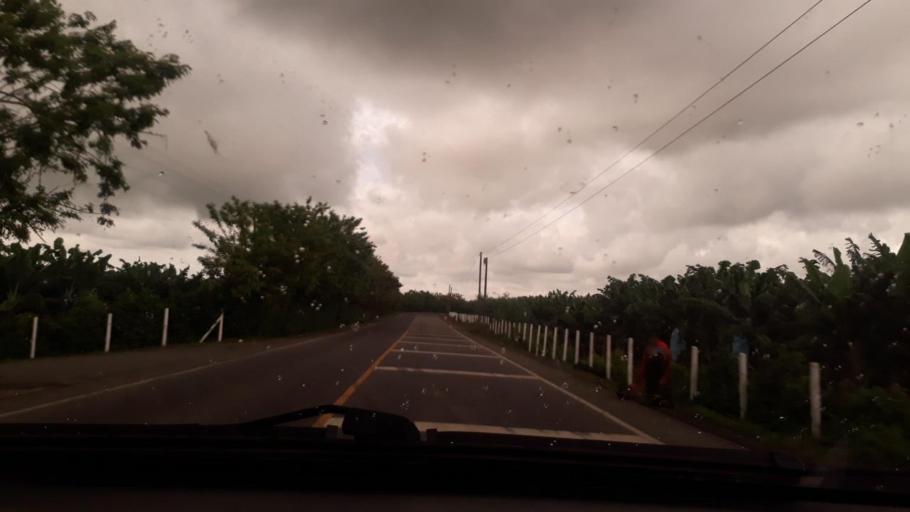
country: HN
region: Cortes
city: Potrerillos
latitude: 15.6402
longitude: -88.4270
